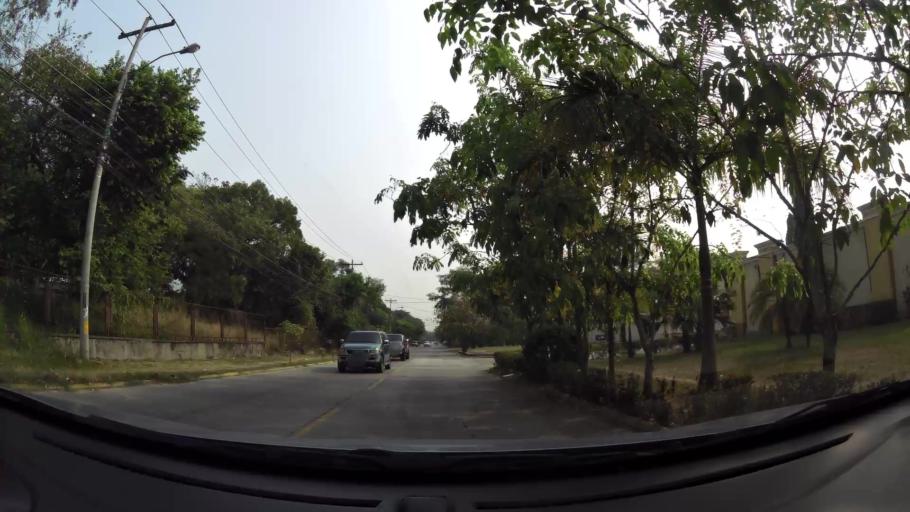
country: HN
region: Cortes
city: El Zapotal del Norte
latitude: 15.5217
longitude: -88.0416
